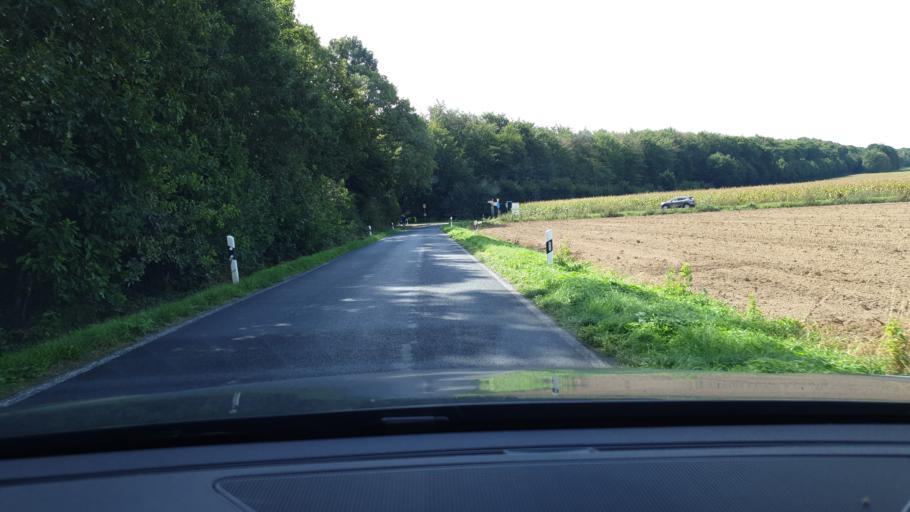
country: NL
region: Gelderland
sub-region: Gemeente Groesbeek
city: De Horst
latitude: 51.7673
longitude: 5.9910
